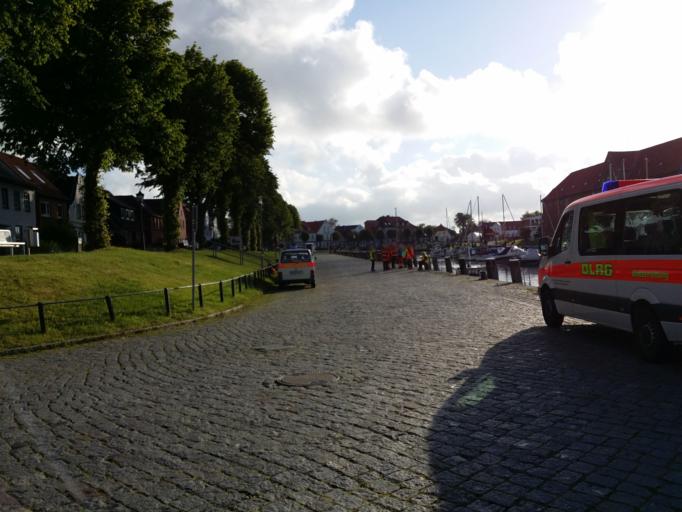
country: DE
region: Schleswig-Holstein
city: Tonning
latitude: 54.3147
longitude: 8.9447
